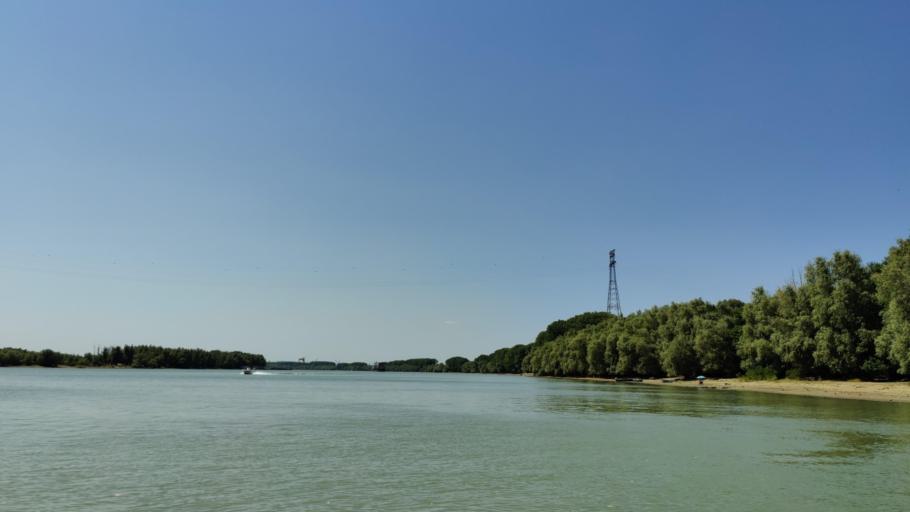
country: RO
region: Tulcea
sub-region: Municipiul Tulcea
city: Tulcea
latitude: 45.2039
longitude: 28.8511
